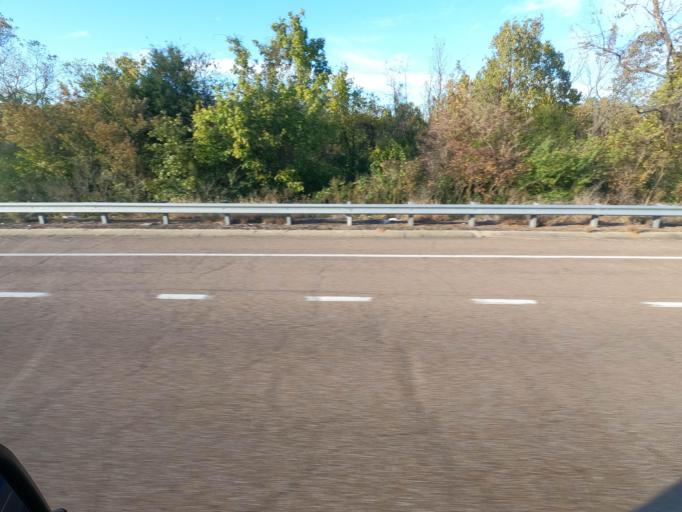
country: US
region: Tennessee
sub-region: Shelby County
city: Millington
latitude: 35.3305
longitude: -89.9055
